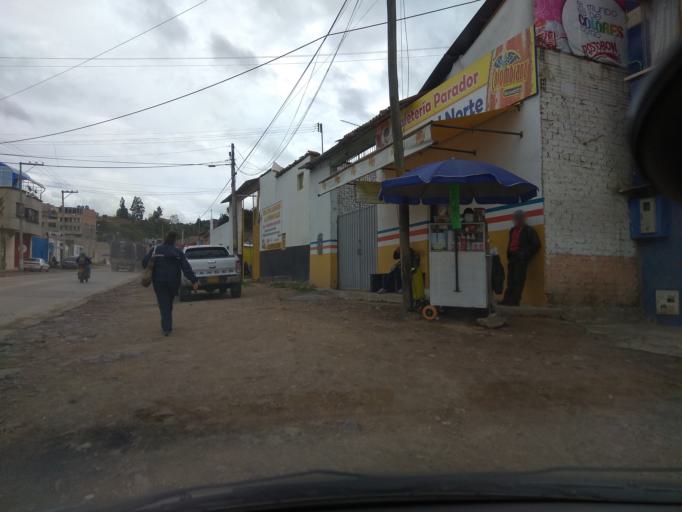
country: CO
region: Boyaca
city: Duitama
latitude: 5.8314
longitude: -73.0239
